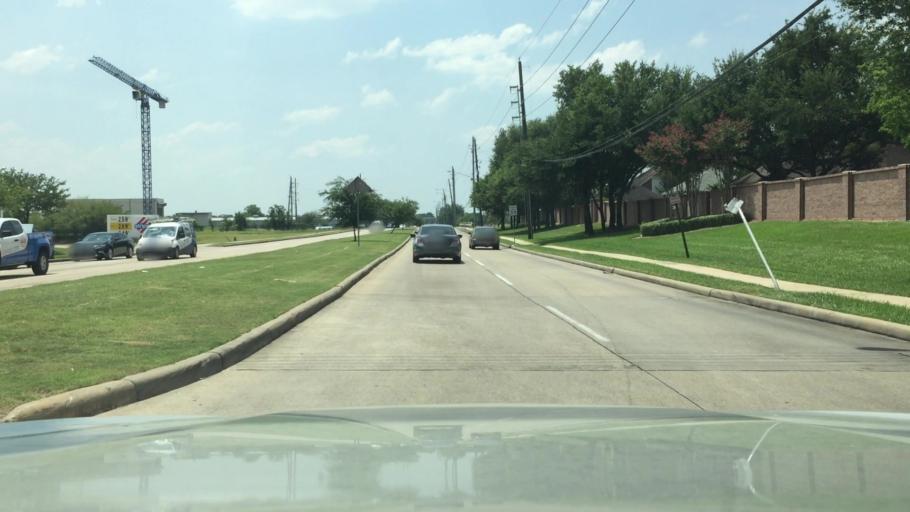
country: US
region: Texas
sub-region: Fort Bend County
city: Meadows Place
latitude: 29.7244
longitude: -95.5925
